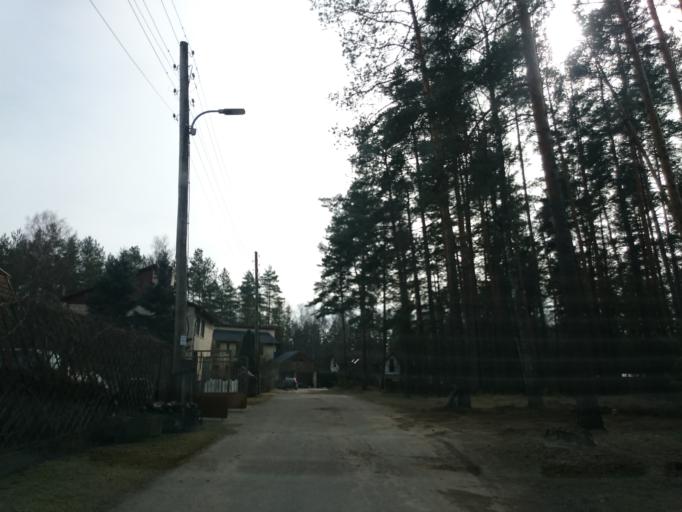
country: LV
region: Riga
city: Bergi
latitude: 57.0066
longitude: 24.3394
